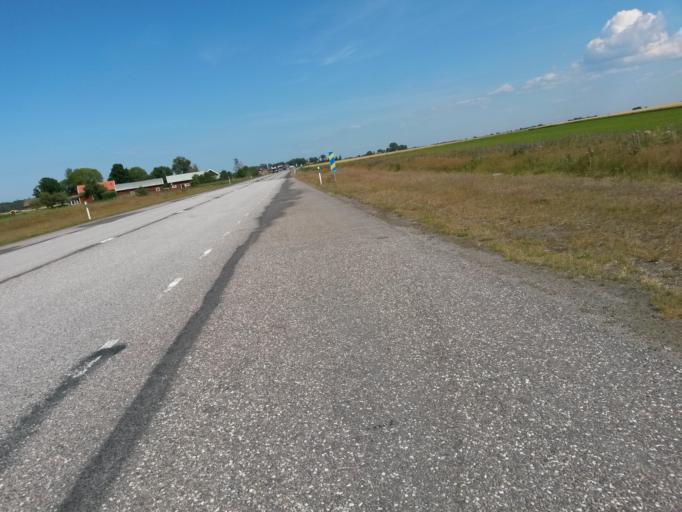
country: SE
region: Vaestra Goetaland
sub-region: Lidkopings Kommun
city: Lidkoping
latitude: 58.4727
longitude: 13.0660
